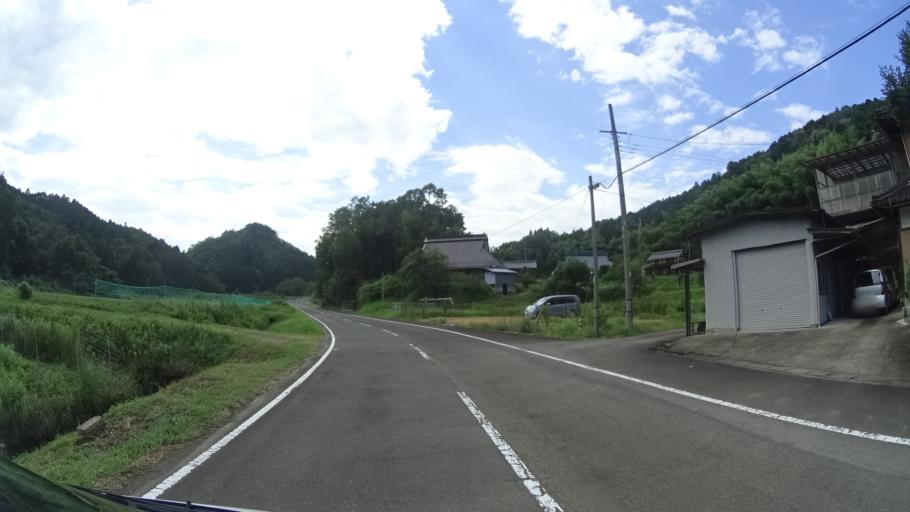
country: JP
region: Kyoto
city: Fukuchiyama
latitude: 35.3700
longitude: 135.1805
